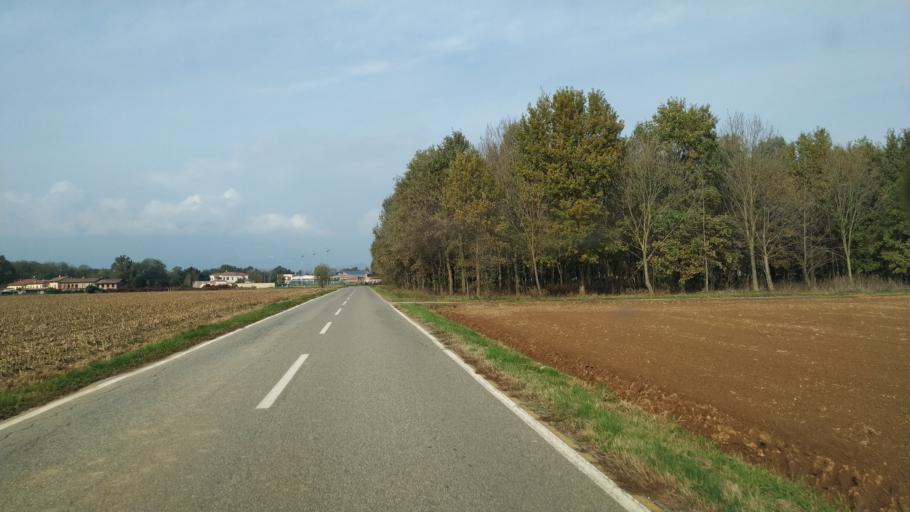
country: IT
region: Piedmont
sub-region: Provincia di Biella
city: Vergnasco
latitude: 45.4778
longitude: 8.0791
